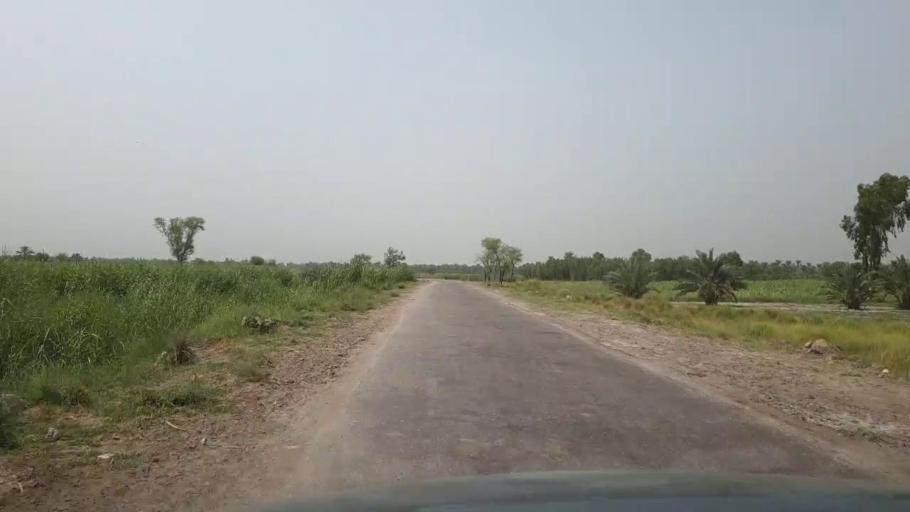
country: PK
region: Sindh
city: Gambat
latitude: 27.3878
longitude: 68.5491
